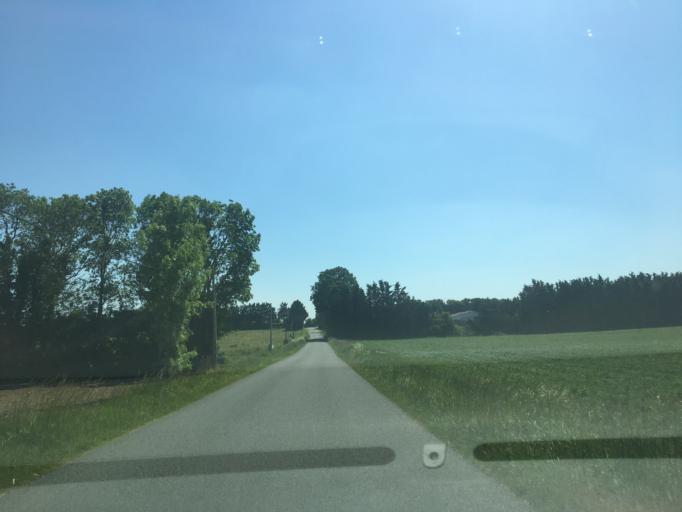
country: FR
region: Poitou-Charentes
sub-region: Departement des Deux-Sevres
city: Beauvoir-sur-Niort
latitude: 46.0802
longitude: -0.5589
